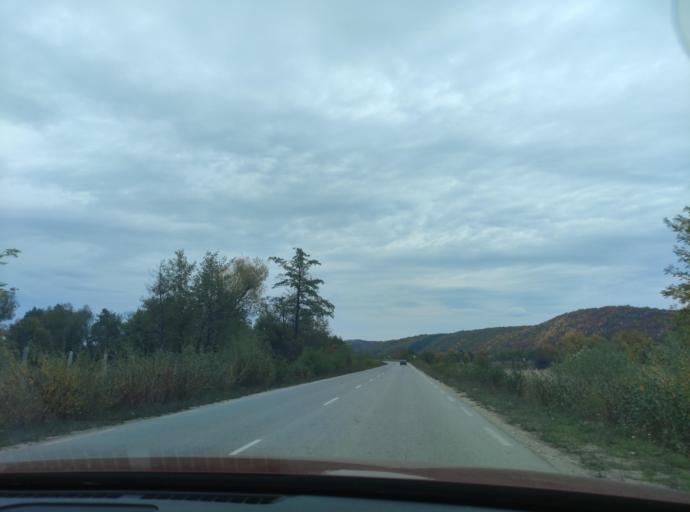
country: BG
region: Montana
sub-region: Obshtina Berkovitsa
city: Berkovitsa
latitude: 43.2463
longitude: 23.1657
